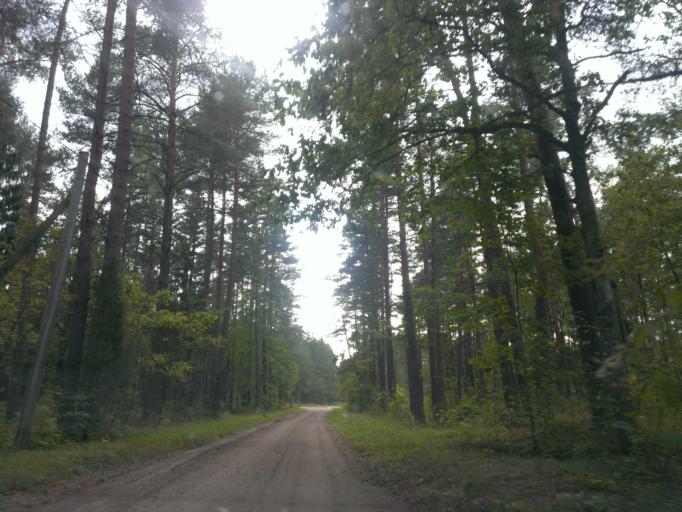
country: LV
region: Incukalns
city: Vangazi
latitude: 57.1113
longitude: 24.5420
